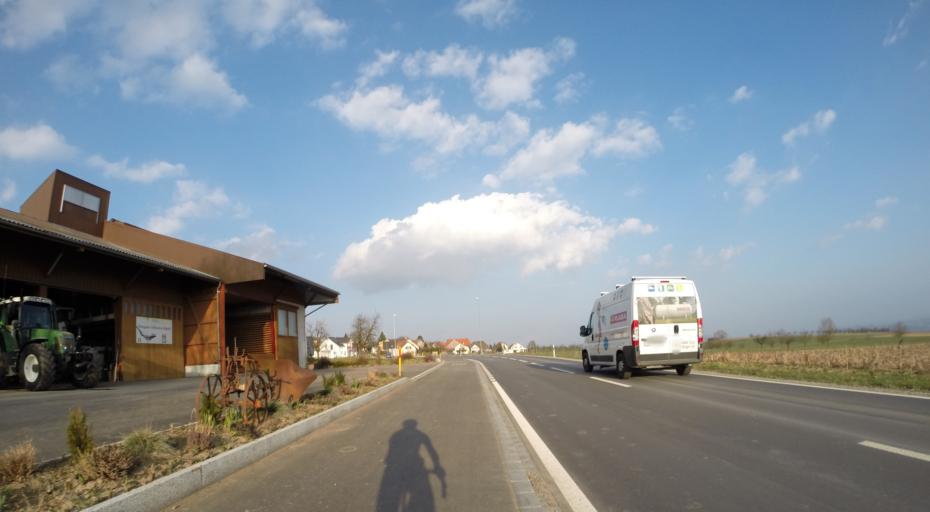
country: CH
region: Thurgau
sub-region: Frauenfeld District
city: Pfyn
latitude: 47.6210
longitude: 8.9342
